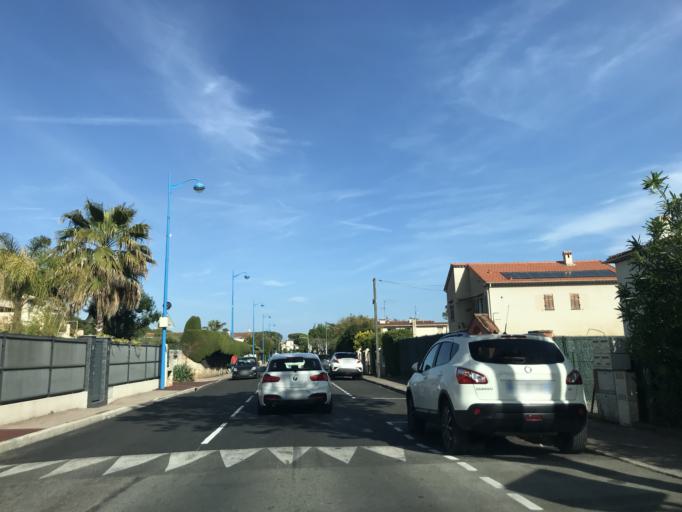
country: FR
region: Provence-Alpes-Cote d'Azur
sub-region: Departement des Alpes-Maritimes
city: Mandelieu-la-Napoule
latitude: 43.5394
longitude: 6.9392
